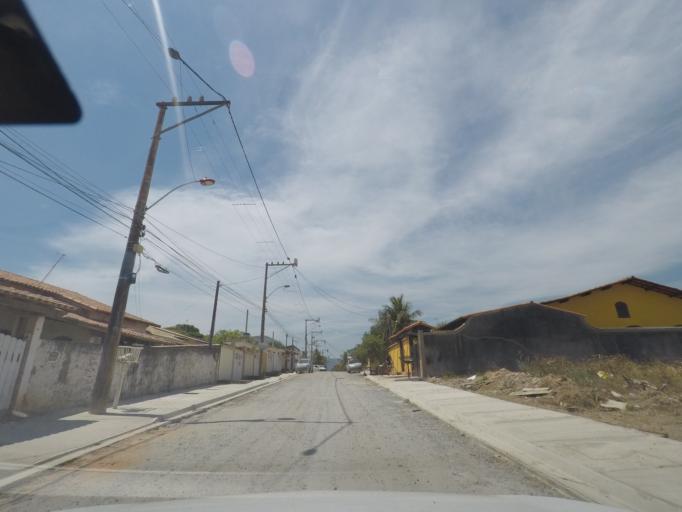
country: BR
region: Rio de Janeiro
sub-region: Marica
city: Marica
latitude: -22.9670
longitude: -42.9549
